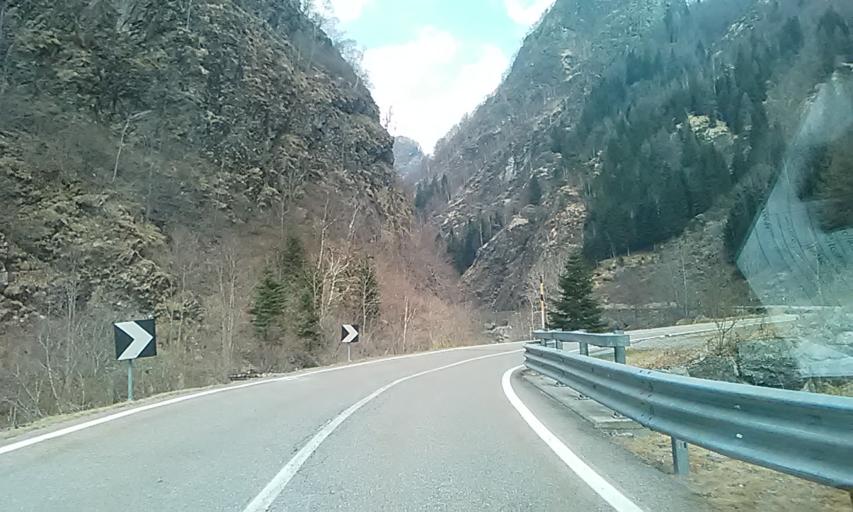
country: IT
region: Piedmont
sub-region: Provincia di Vercelli
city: Cervatto
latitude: 45.8876
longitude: 8.1784
